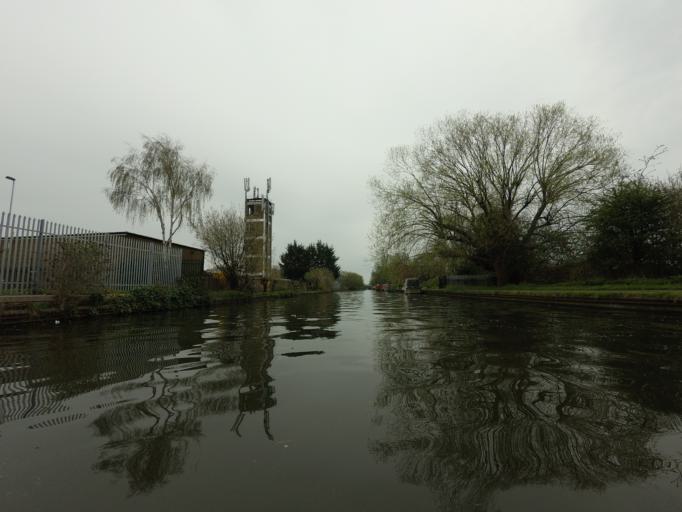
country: GB
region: England
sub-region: Greater London
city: Acton
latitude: 51.5358
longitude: -0.2660
